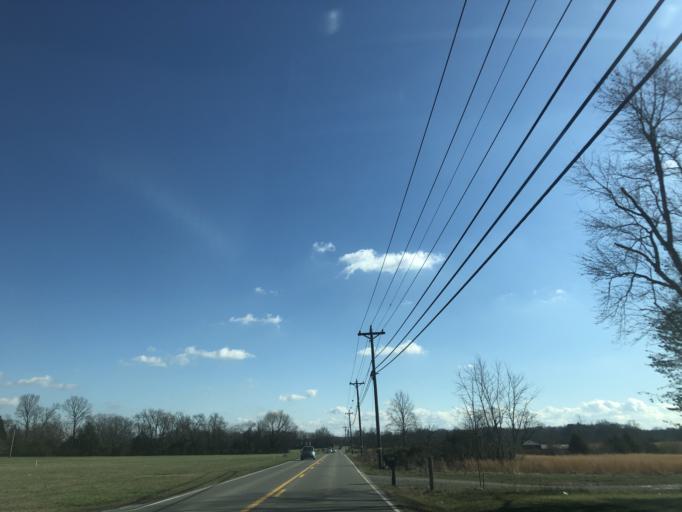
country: US
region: Tennessee
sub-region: Rutherford County
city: Murfreesboro
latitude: 35.9684
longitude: -86.3952
